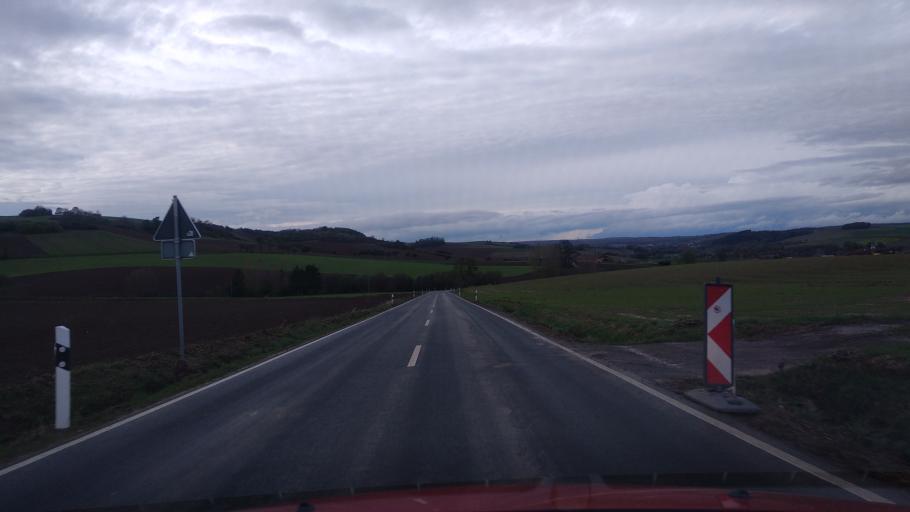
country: DE
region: North Rhine-Westphalia
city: Brakel
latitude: 51.6728
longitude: 9.2327
